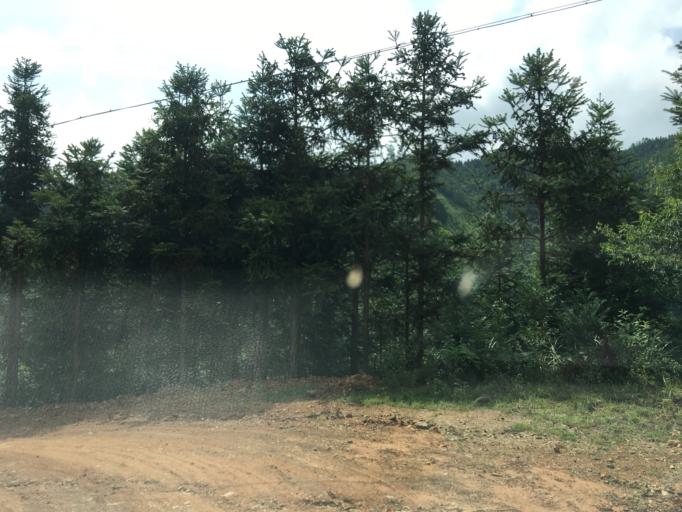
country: CN
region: Guangxi Zhuangzu Zizhiqu
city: Xinzhou
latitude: 24.8652
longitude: 105.8547
